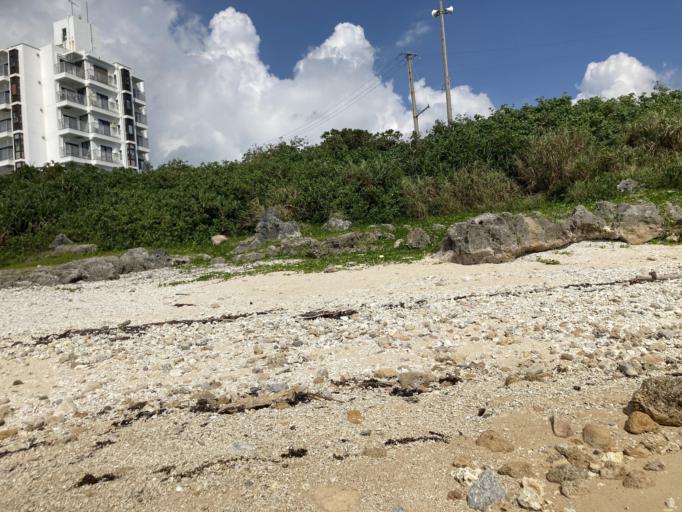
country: JP
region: Okinawa
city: Itoman
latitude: 26.1281
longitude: 127.7748
